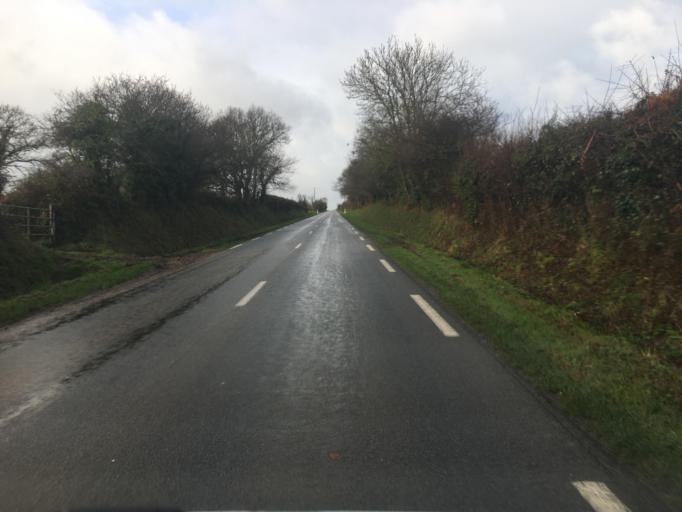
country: FR
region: Lower Normandy
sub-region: Departement de la Manche
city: Saint-Pierre-Eglise
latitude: 49.6690
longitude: -1.3670
